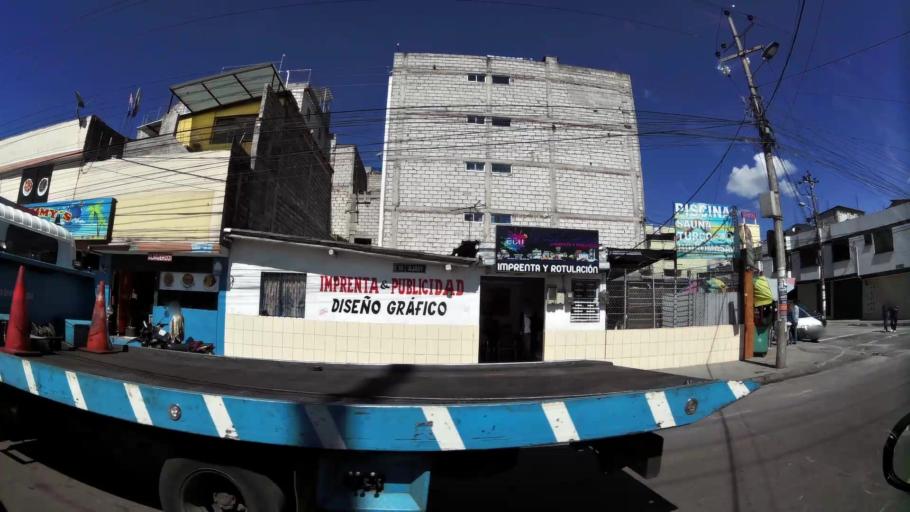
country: EC
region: Pichincha
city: Quito
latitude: -0.2583
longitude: -78.5413
